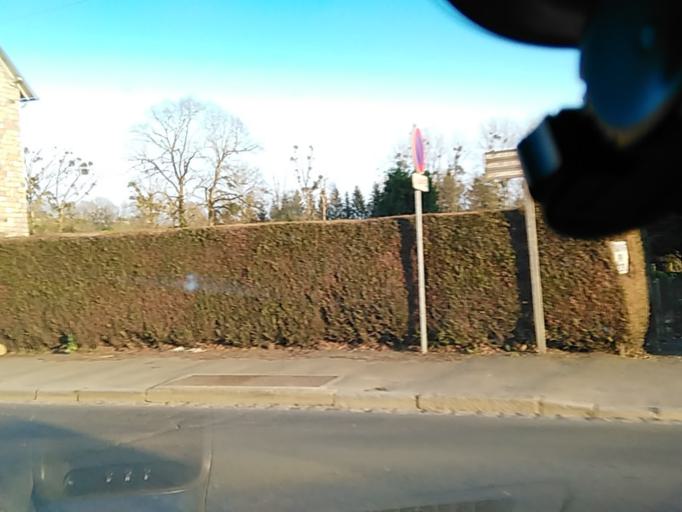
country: FR
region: Lower Normandy
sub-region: Departement de l'Orne
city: Domfront
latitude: 48.5902
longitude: -0.6594
